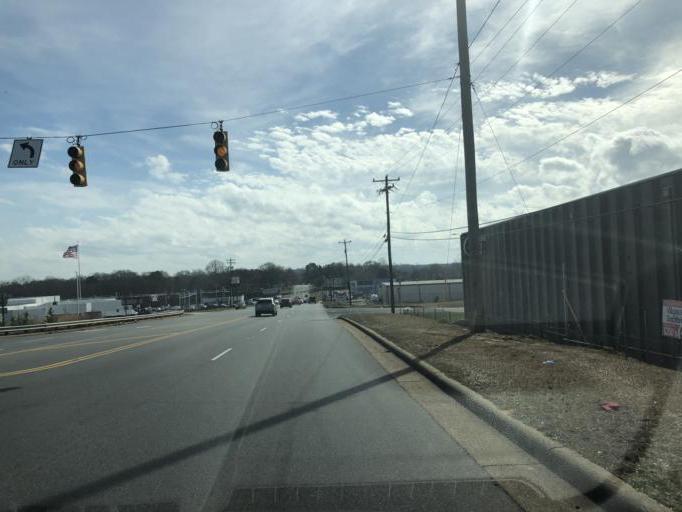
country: US
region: North Carolina
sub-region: Gaston County
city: Lowell
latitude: 35.2591
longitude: -81.1054
